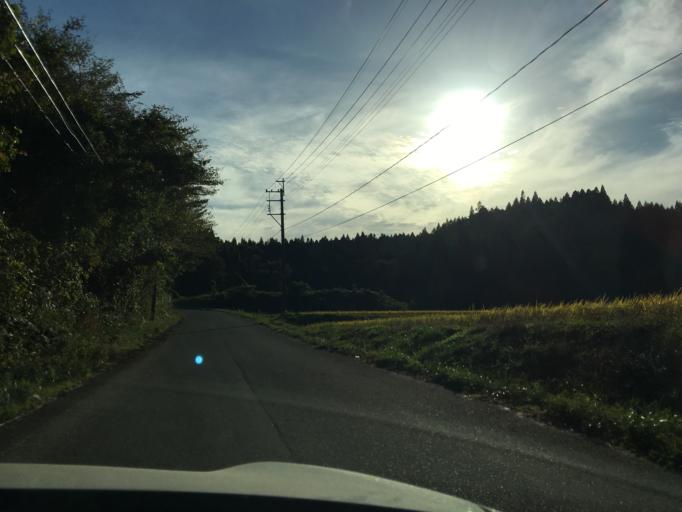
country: JP
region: Fukushima
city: Ishikawa
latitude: 37.2360
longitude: 140.6120
